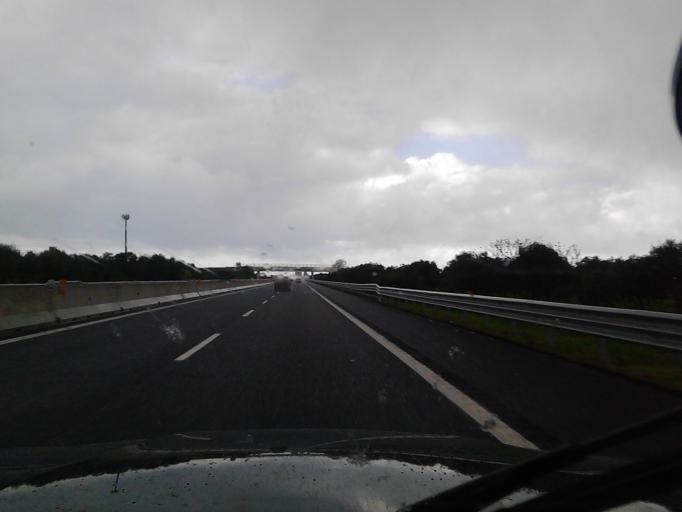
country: IT
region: Apulia
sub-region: Provincia di Bari
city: Giovinazzo
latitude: 41.1589
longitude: 16.6373
